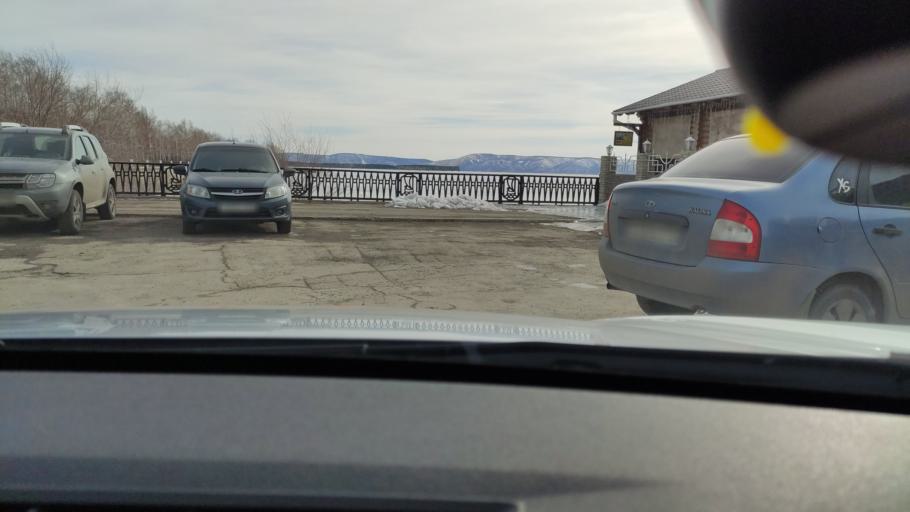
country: RU
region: Samara
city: Tol'yatti
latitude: 53.4944
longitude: 49.2692
